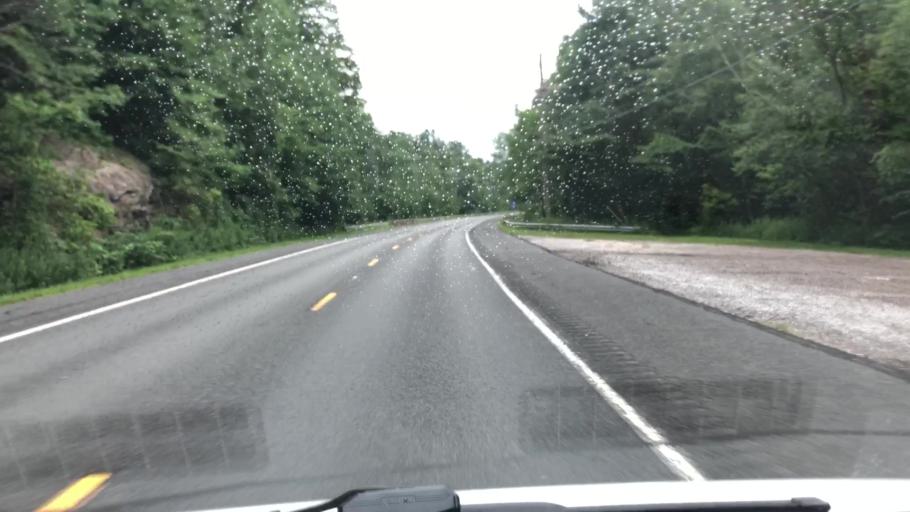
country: US
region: Massachusetts
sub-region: Berkshire County
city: Lanesborough
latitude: 42.5495
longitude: -73.2342
